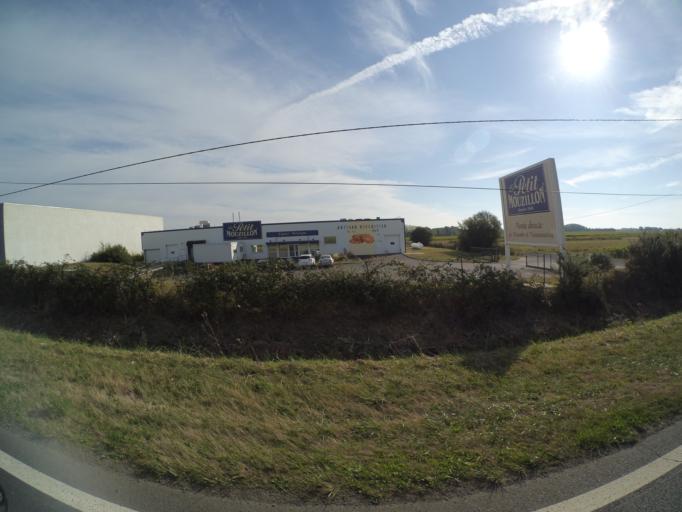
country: FR
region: Pays de la Loire
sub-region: Departement de la Loire-Atlantique
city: Mouzillon
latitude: 47.1228
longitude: -1.2826
